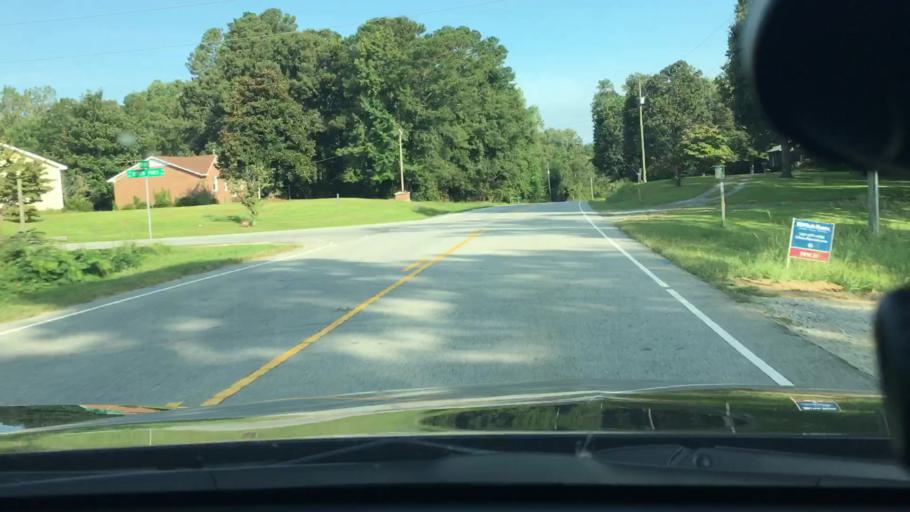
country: US
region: North Carolina
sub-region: Edgecombe County
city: Pinetops
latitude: 35.7184
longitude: -77.5278
